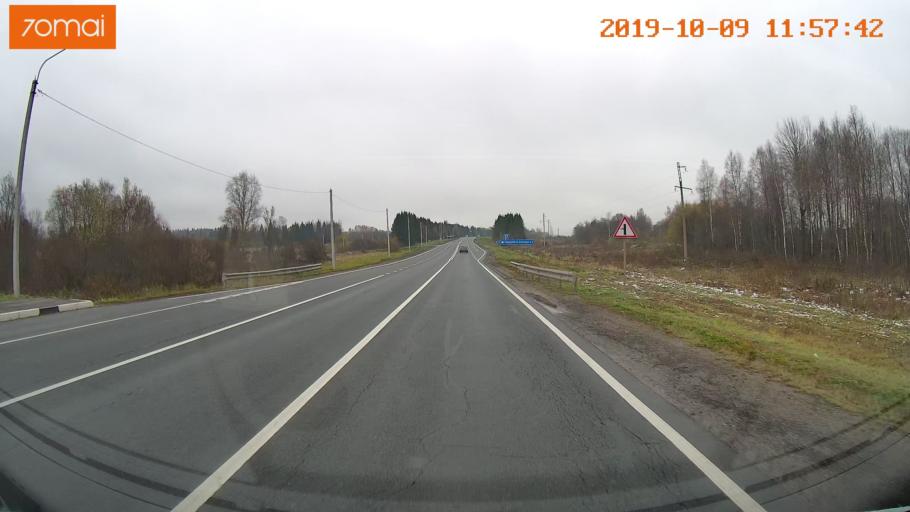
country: RU
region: Vologda
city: Gryazovets
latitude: 58.7287
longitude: 40.2941
